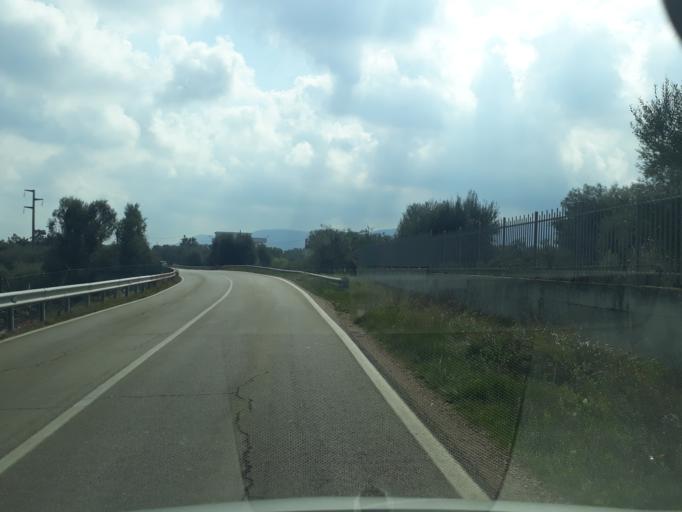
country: IT
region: Apulia
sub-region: Provincia di Brindisi
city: Fasano
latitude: 40.8243
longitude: 17.3717
